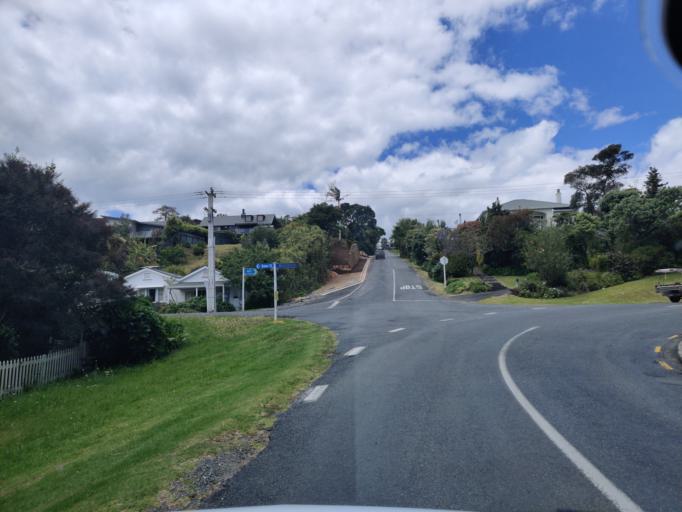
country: NZ
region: Northland
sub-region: Far North District
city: Paihia
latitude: -35.2635
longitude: 174.1236
